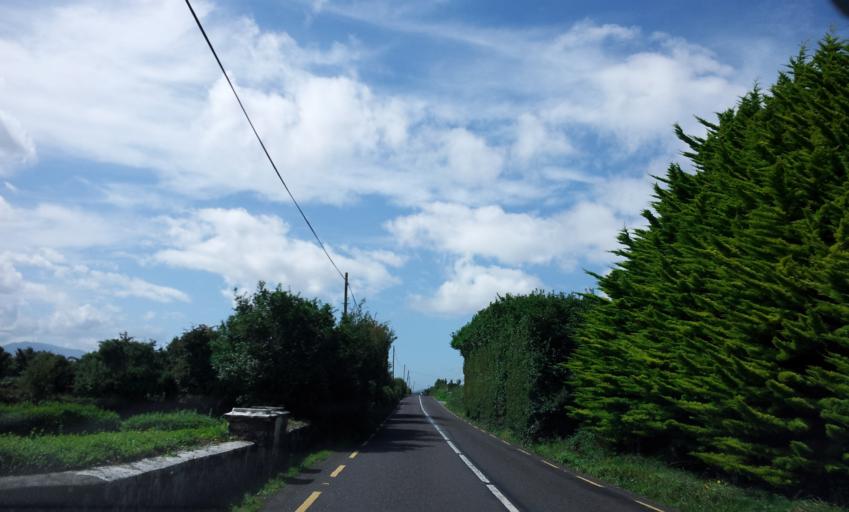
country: IE
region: Munster
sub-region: Ciarrai
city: Killorglin
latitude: 52.1631
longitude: -9.8389
